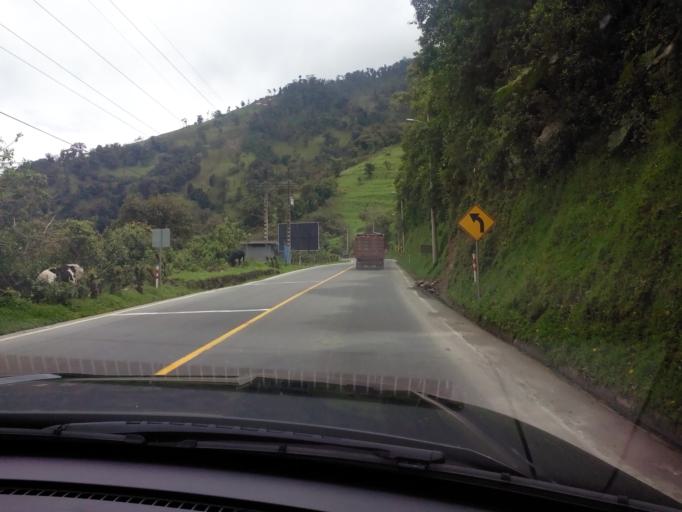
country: EC
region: Pichincha
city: Sangolqui
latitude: -0.4114
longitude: -78.0287
